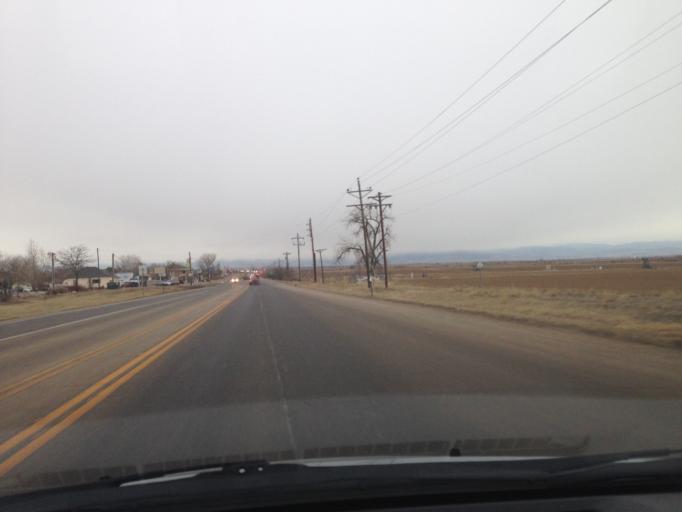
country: US
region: Colorado
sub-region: Weld County
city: Dacono
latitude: 40.0878
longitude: -104.9316
